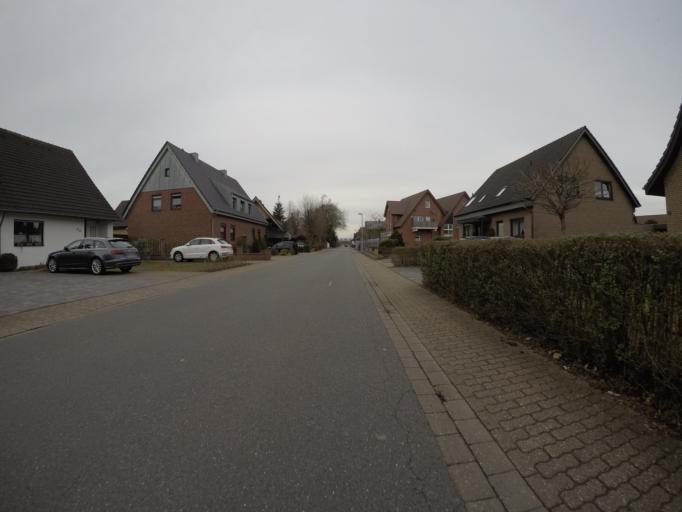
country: DE
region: North Rhine-Westphalia
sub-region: Regierungsbezirk Dusseldorf
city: Bocholt
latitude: 51.8190
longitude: 6.6269
